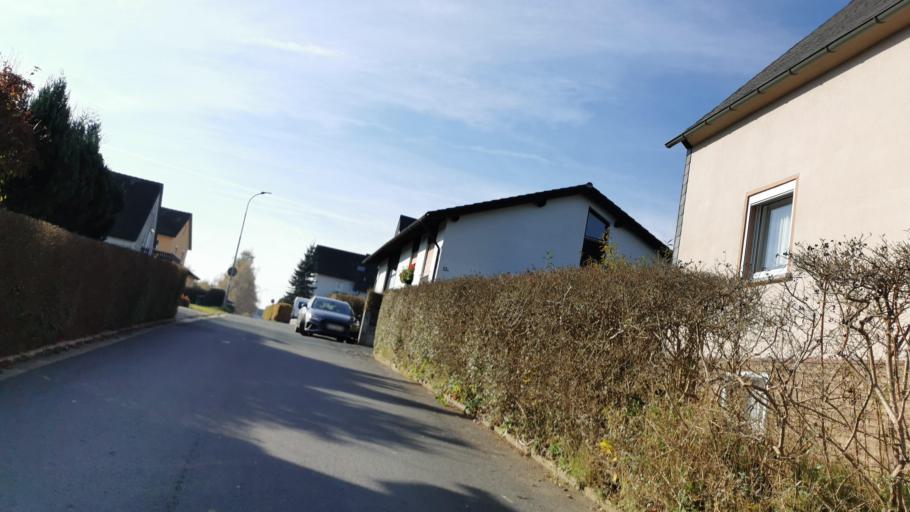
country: DE
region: Bavaria
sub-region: Upper Franconia
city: Nordhalben
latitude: 50.3696
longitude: 11.5089
